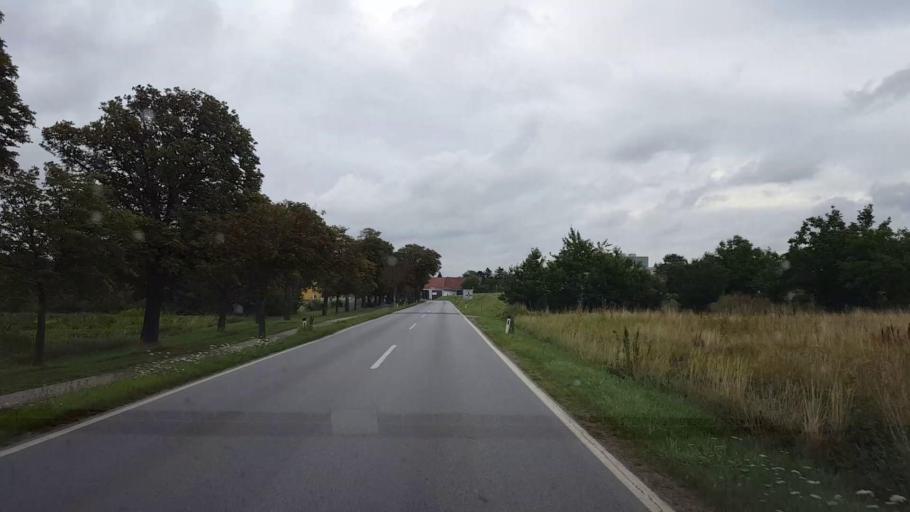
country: AT
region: Lower Austria
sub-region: Politischer Bezirk Wien-Umgebung
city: Rauchenwarth
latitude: 48.0841
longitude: 16.5211
